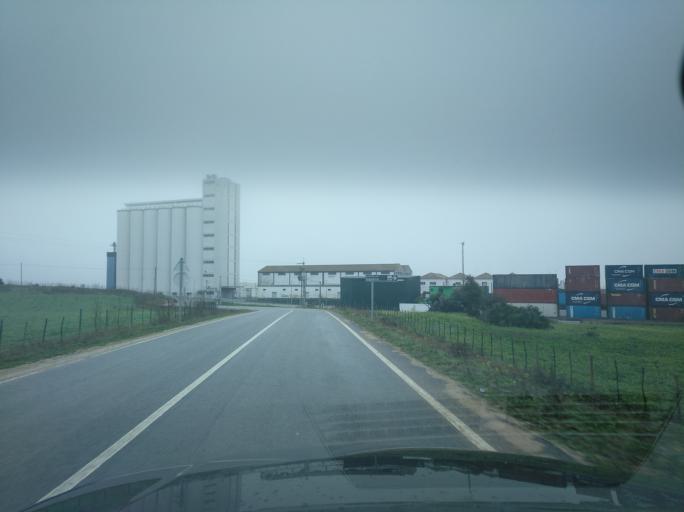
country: PT
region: Portalegre
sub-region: Elvas
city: Elvas
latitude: 38.8972
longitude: -7.1400
